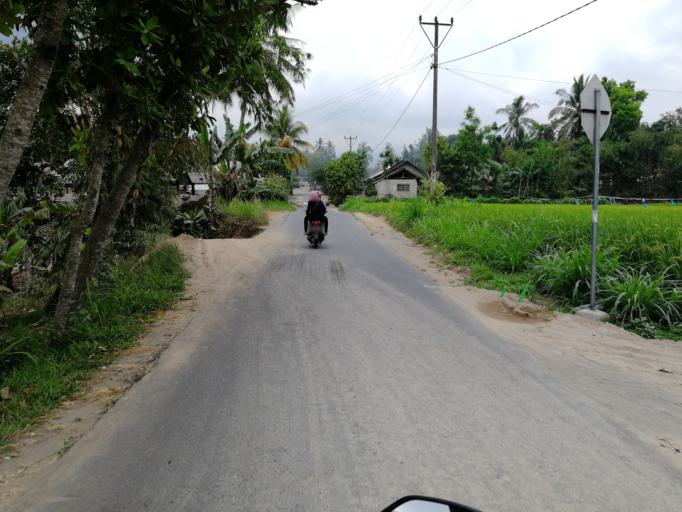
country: ID
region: West Nusa Tenggara
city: Pediti
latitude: -8.5651
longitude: 116.3308
